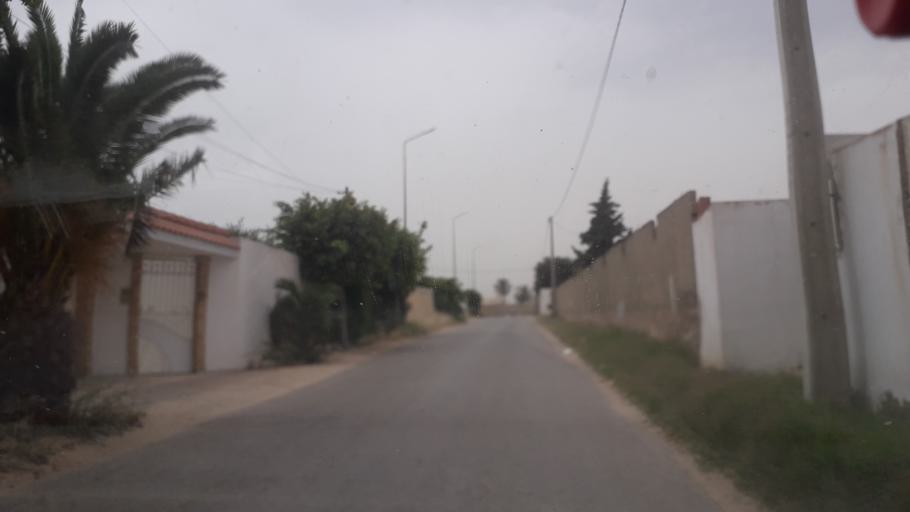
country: TN
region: Safaqis
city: Al Qarmadah
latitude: 34.7917
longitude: 10.7630
